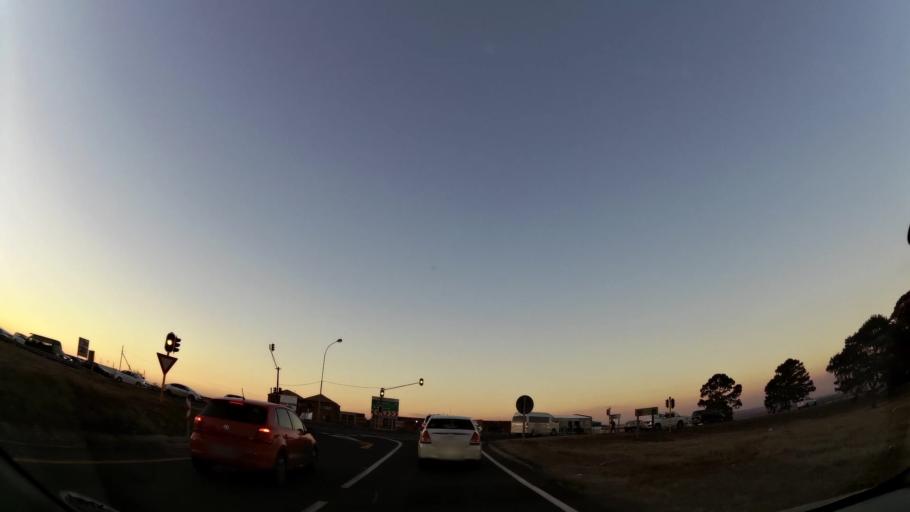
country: ZA
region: Mpumalanga
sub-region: Nkangala District Municipality
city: Witbank
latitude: -25.8873
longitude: 29.2699
